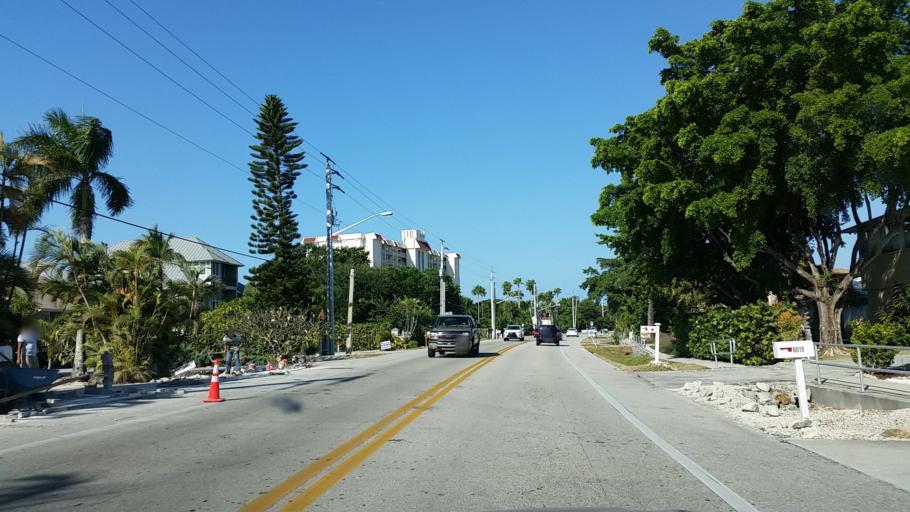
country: US
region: Florida
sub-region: Lee County
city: Fort Myers Beach
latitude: 26.4048
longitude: -81.8922
